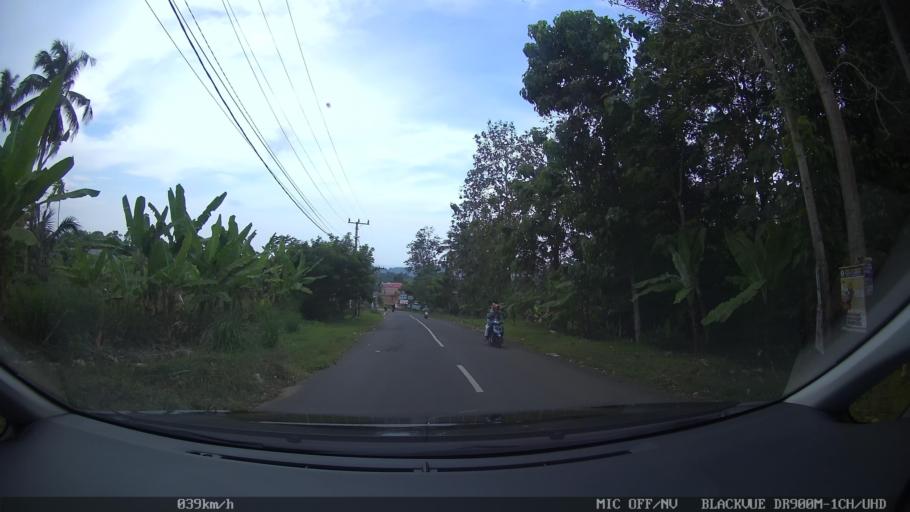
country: ID
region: Lampung
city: Bandarlampung
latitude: -5.4222
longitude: 105.1938
